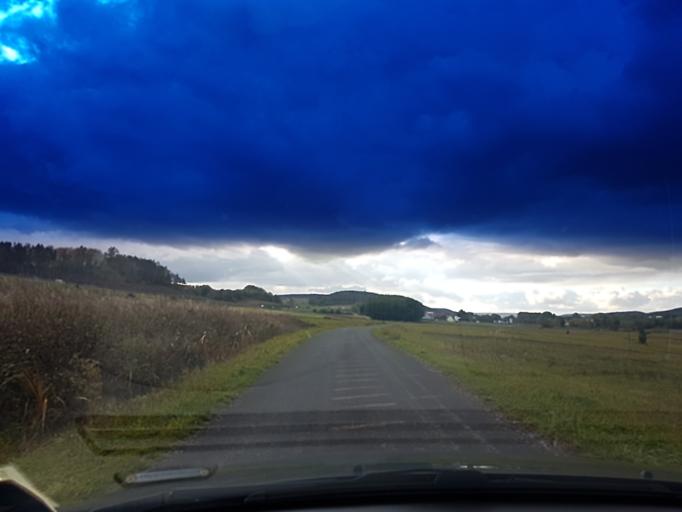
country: DE
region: Bavaria
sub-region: Regierungsbezirk Mittelfranken
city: Burghaslach
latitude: 49.7609
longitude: 10.5849
